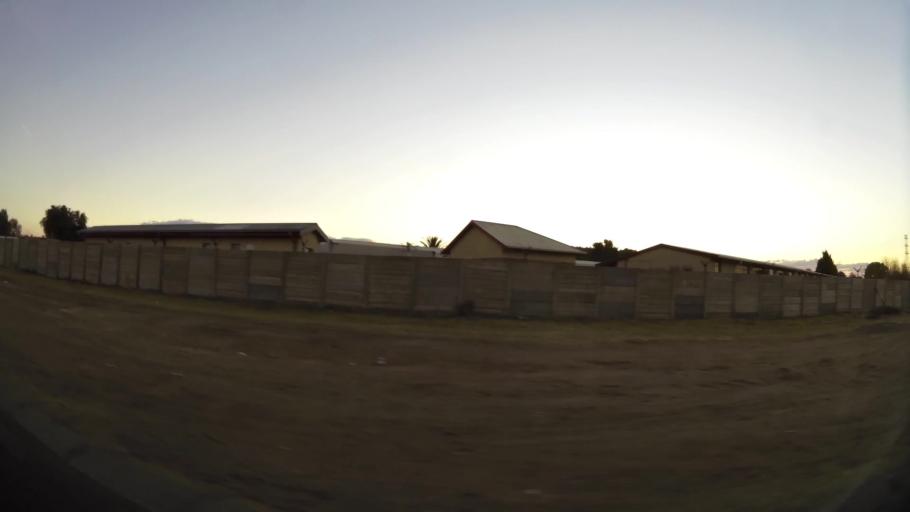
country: ZA
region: Northern Cape
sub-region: Frances Baard District Municipality
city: Kimberley
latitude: -28.7136
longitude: 24.7724
